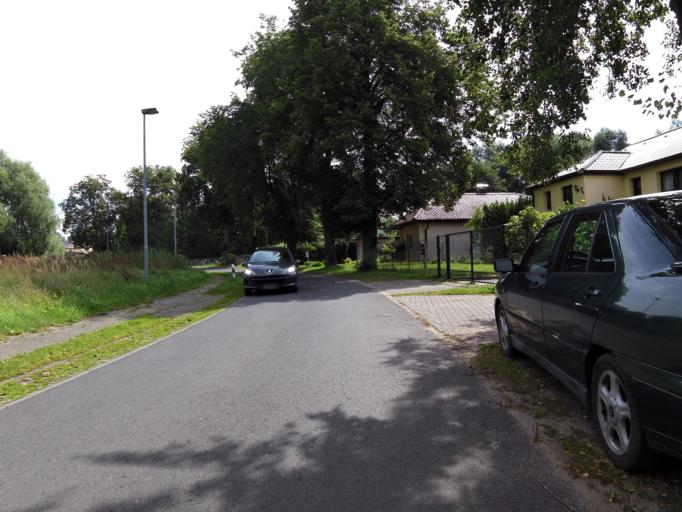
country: DE
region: Brandenburg
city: Lychen
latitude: 53.2897
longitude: 13.3318
